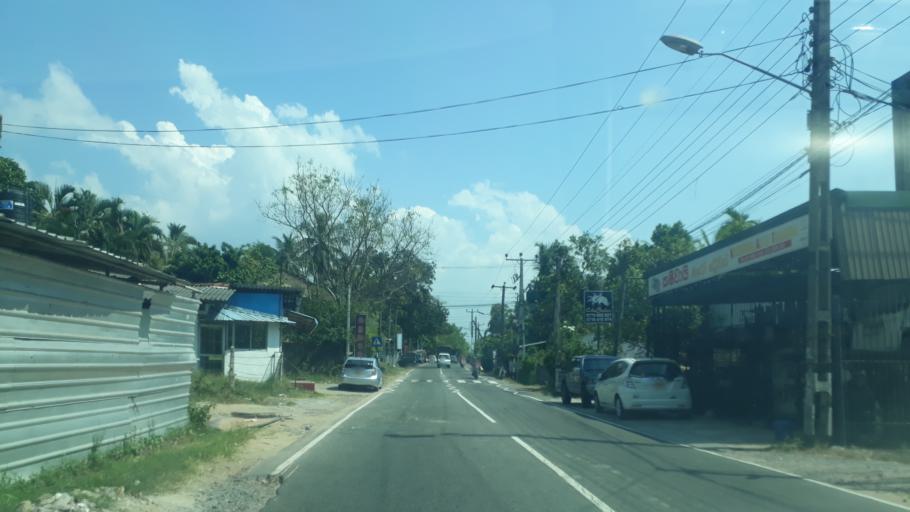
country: LK
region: Western
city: Gampaha
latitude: 7.0869
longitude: 80.0076
